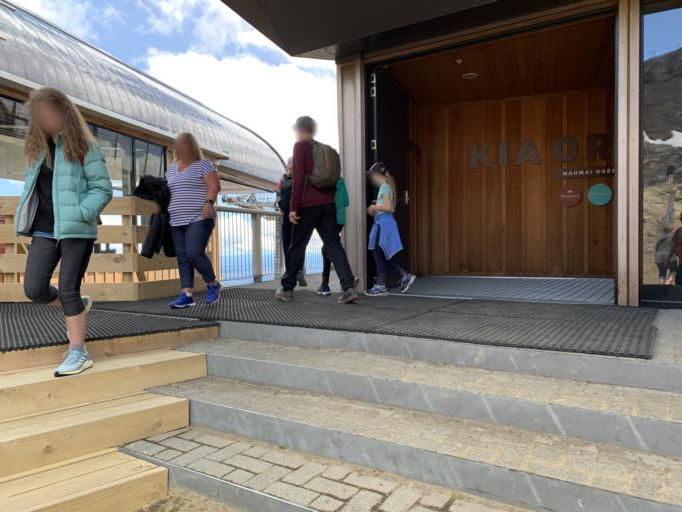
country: NZ
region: Manawatu-Wanganui
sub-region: Ruapehu District
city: Waiouru
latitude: -39.2523
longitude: 175.5644
